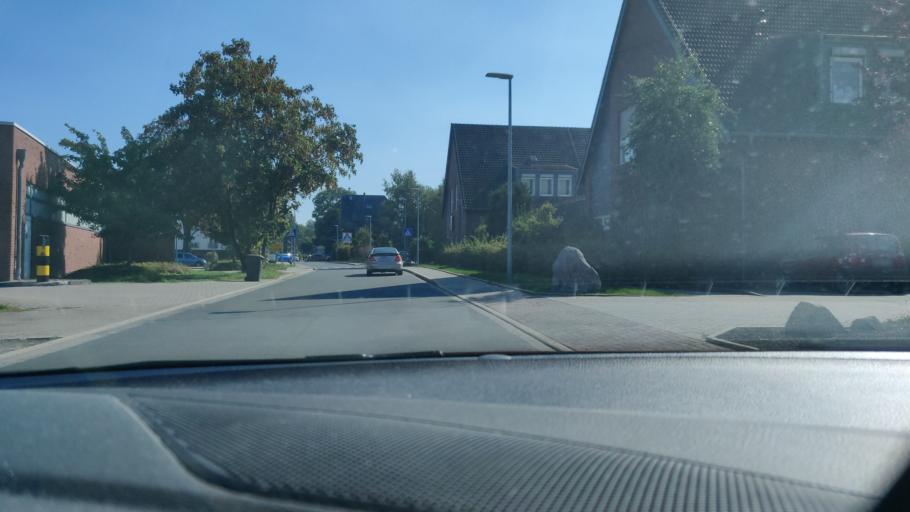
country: DE
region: North Rhine-Westphalia
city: Sprockhovel
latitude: 51.3662
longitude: 7.2439
